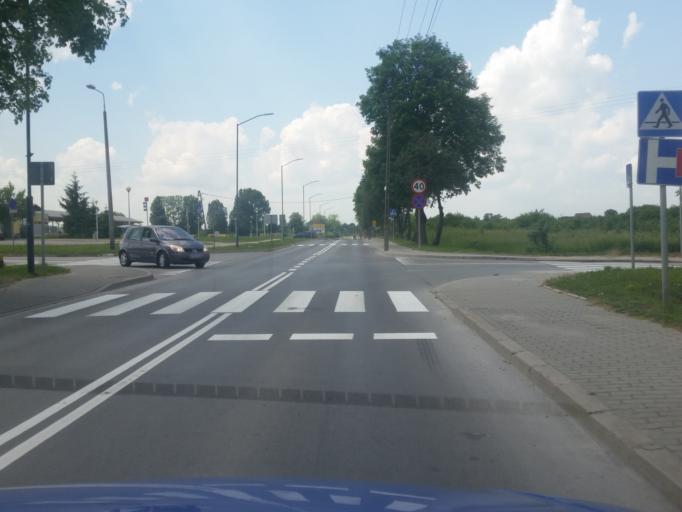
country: PL
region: Swietokrzyskie
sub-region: Powiat buski
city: Busko-Zdroj
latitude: 50.4611
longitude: 20.7076
